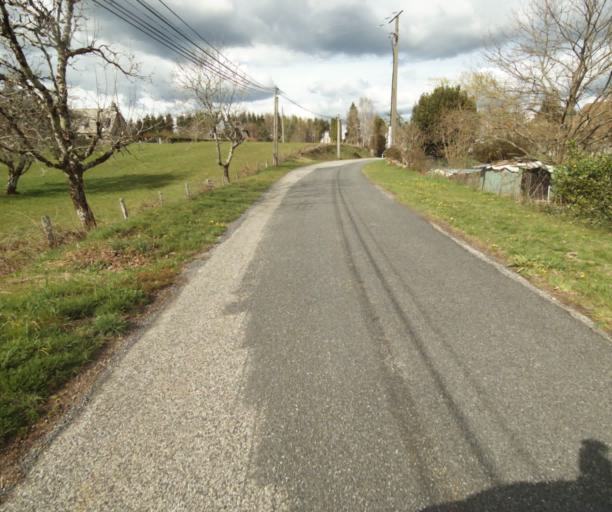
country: FR
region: Limousin
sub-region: Departement de la Correze
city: Argentat
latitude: 45.2112
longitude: 1.9667
